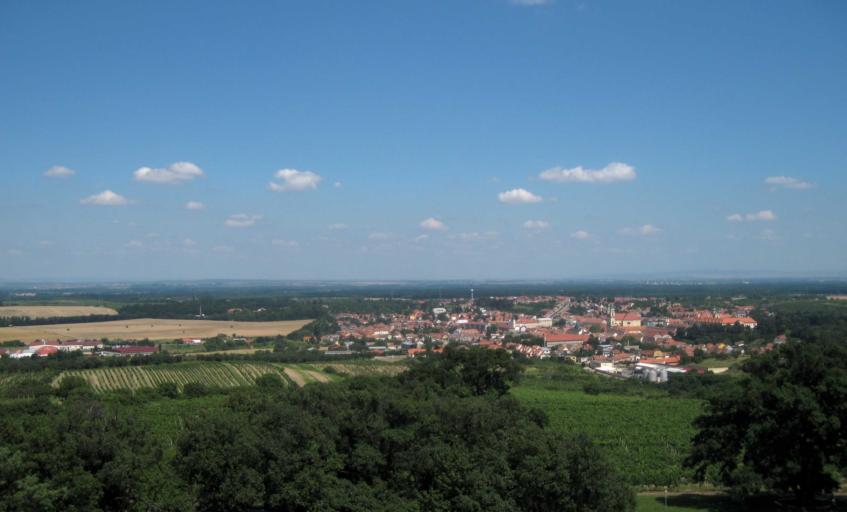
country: CZ
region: South Moravian
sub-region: Okres Breclav
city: Valtice
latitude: 48.7370
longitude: 16.7363
